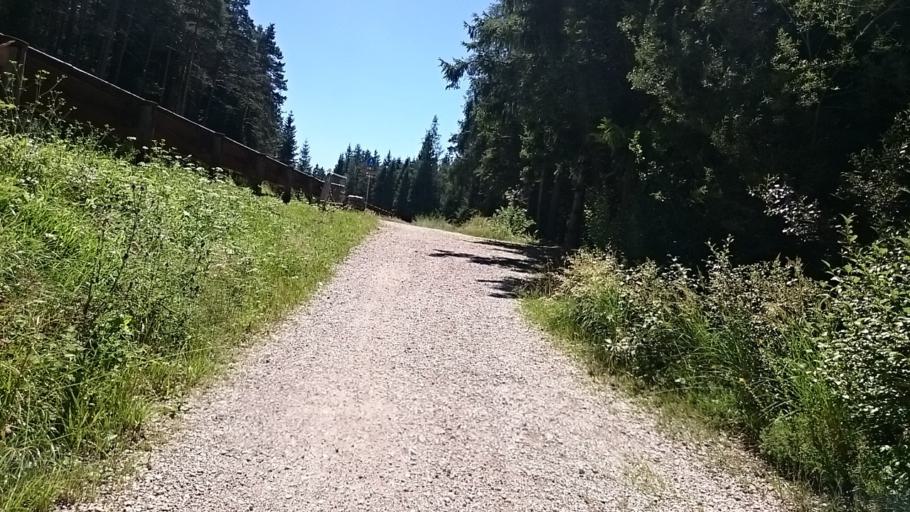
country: IT
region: Veneto
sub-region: Provincia di Belluno
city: San Vito
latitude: 46.4940
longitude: 12.1797
